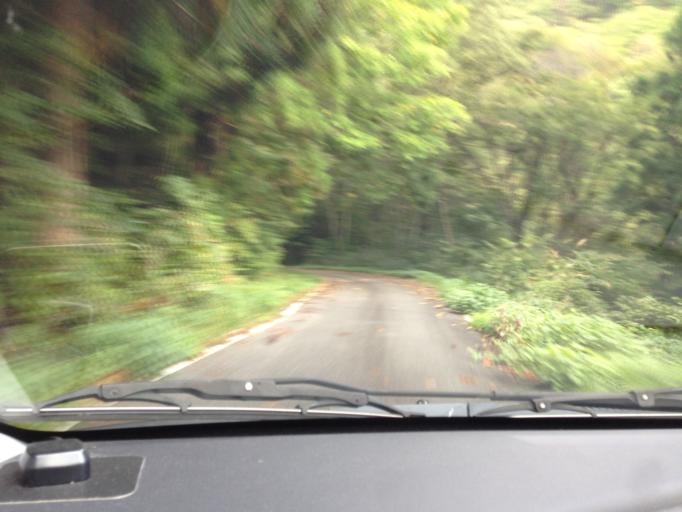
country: JP
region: Fukushima
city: Kitakata
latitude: 37.3652
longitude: 139.6096
